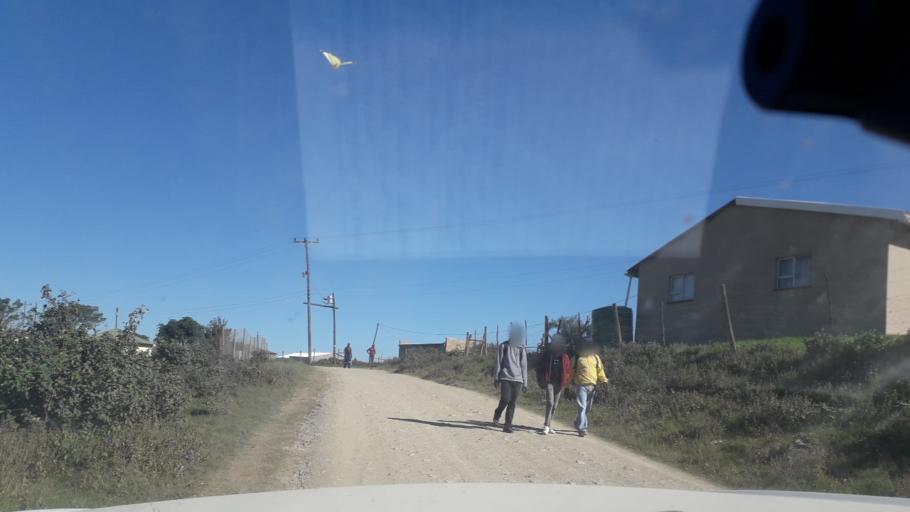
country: ZA
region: Eastern Cape
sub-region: Amathole District Municipality
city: Komga
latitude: -32.7683
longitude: 27.9457
